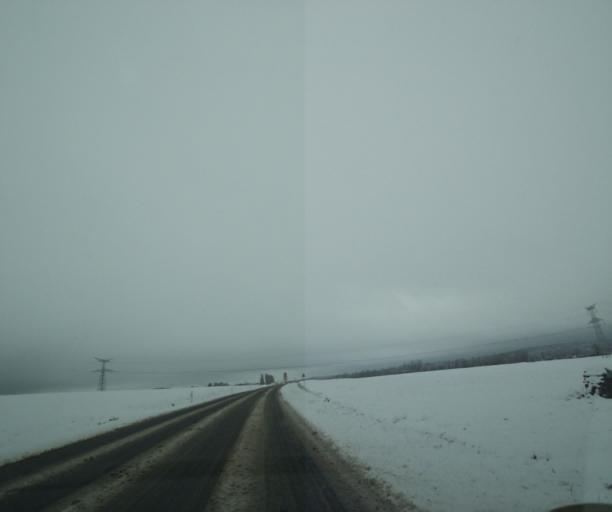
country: FR
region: Champagne-Ardenne
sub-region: Departement de la Haute-Marne
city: Wassy
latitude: 48.5216
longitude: 4.9330
